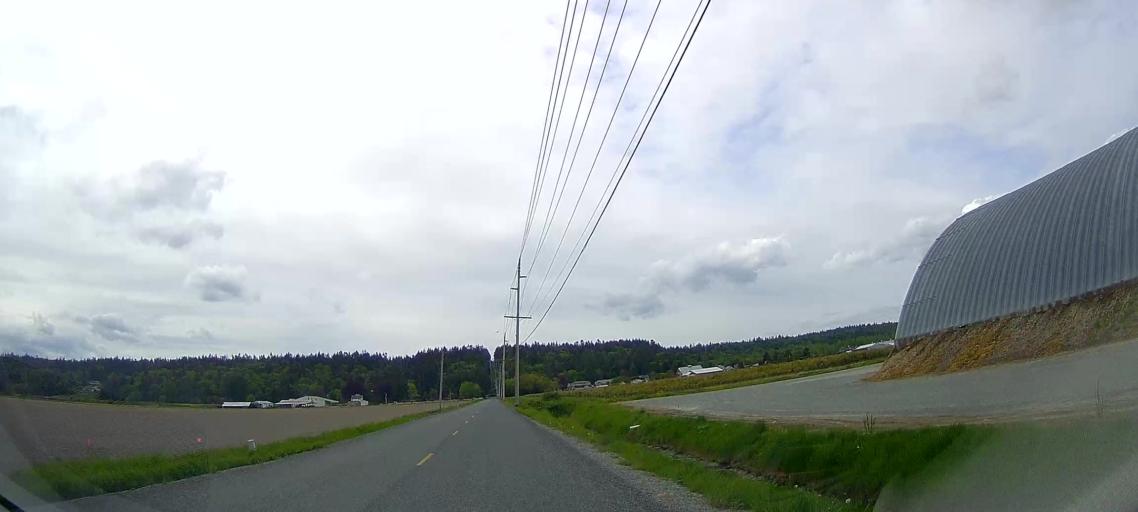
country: US
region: Washington
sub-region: Skagit County
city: Anacortes
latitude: 48.4209
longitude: -122.4905
